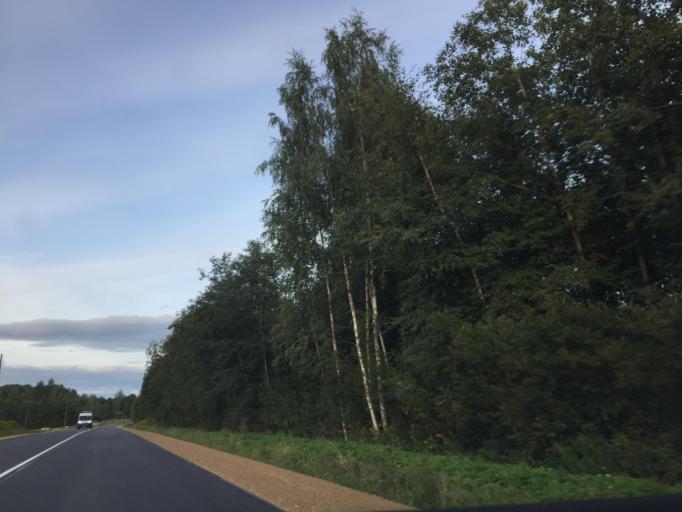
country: LV
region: Viesite
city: Viesite
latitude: 56.3900
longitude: 25.6762
